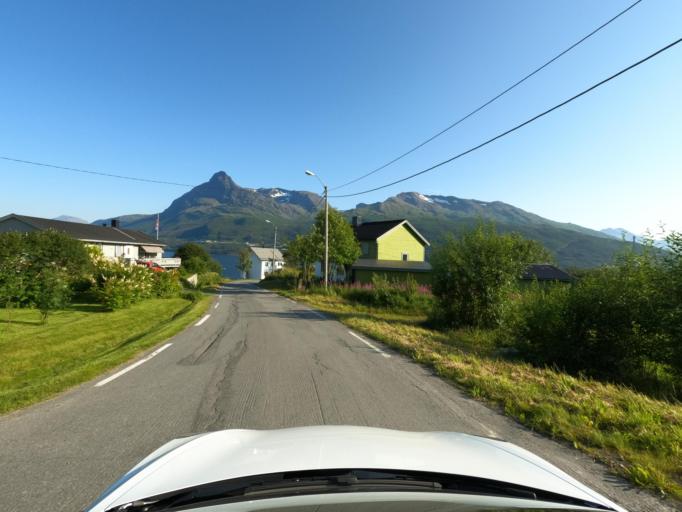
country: NO
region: Nordland
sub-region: Narvik
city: Narvik
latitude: 68.4712
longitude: 17.5034
